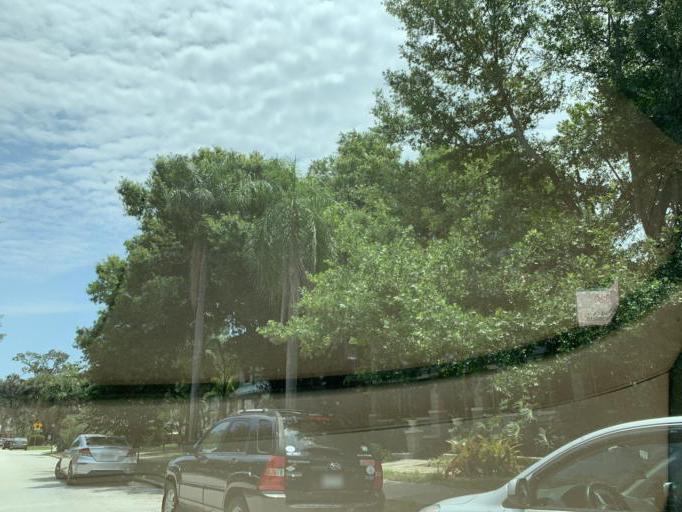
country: US
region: Florida
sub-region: Pinellas County
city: Saint Petersburg
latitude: 27.7794
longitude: -82.6441
